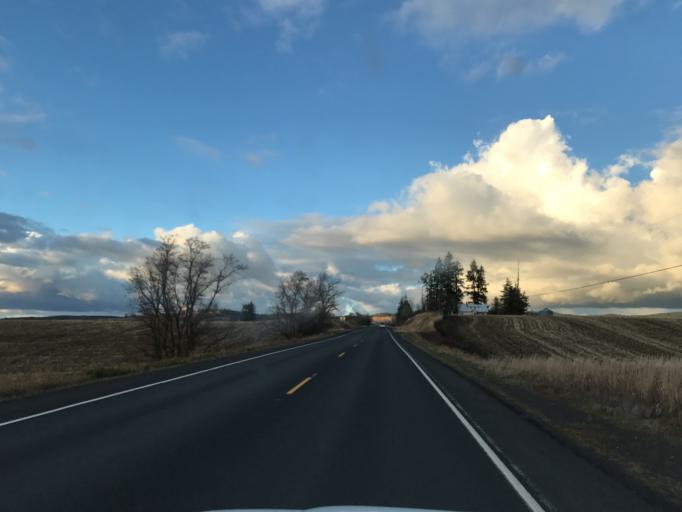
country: US
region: Idaho
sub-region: Latah County
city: Moscow
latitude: 46.7586
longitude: -117.0017
